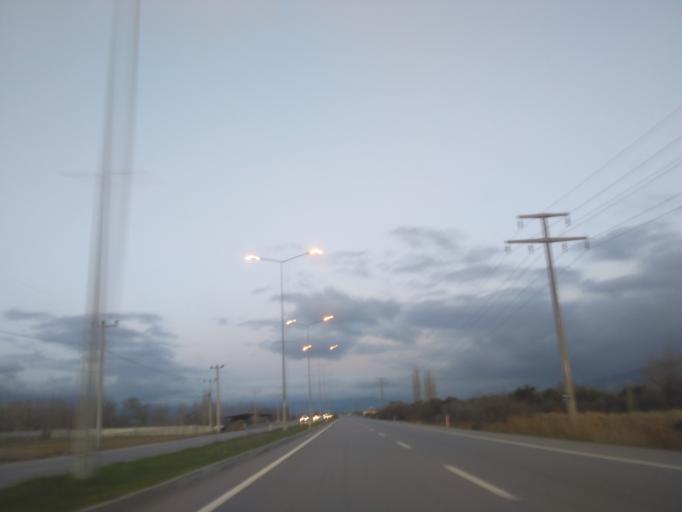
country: TR
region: Balikesir
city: Burhaniye
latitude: 39.5179
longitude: 26.9870
